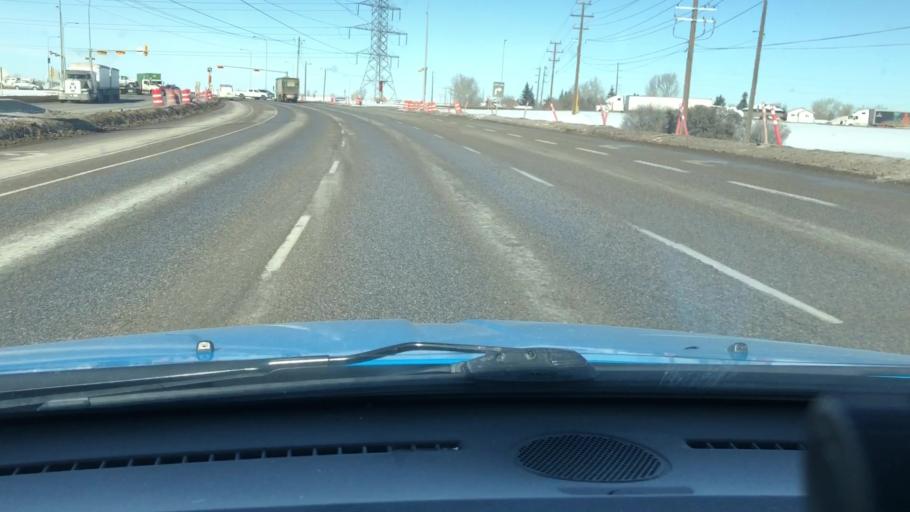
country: CA
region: Alberta
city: Calgary
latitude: 51.0137
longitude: -114.0017
